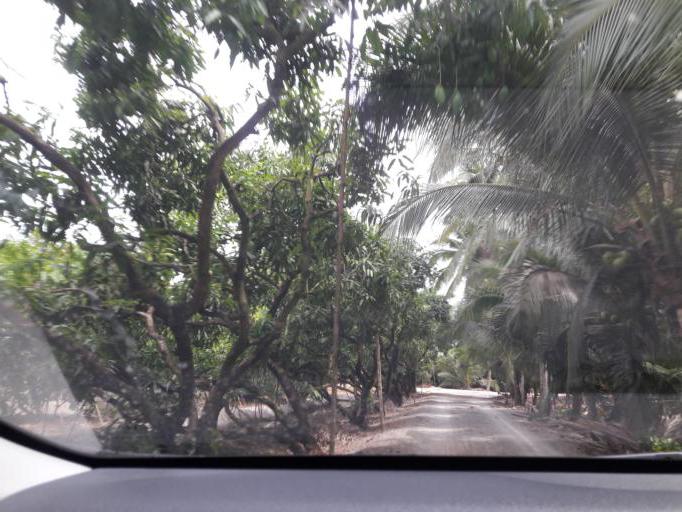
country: TH
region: Ratchaburi
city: Damnoen Saduak
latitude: 13.5593
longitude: 99.9917
